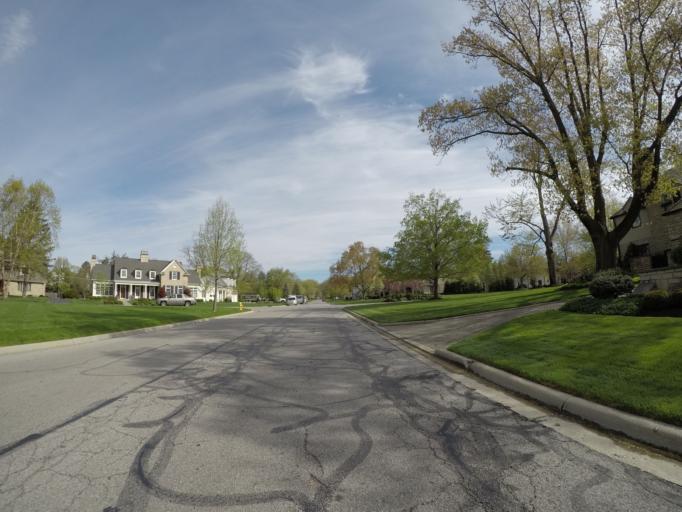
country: US
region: Ohio
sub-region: Franklin County
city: Upper Arlington
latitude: 40.0094
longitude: -83.0765
